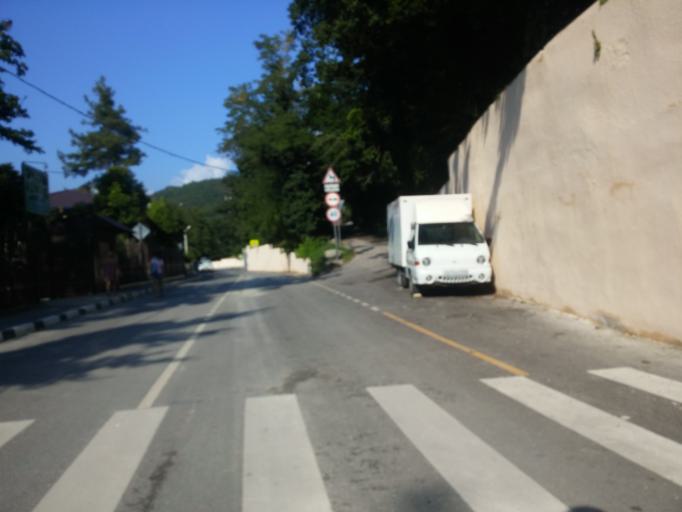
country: RU
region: Krasnodarskiy
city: Divnomorskoye
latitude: 44.4644
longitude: 38.1586
